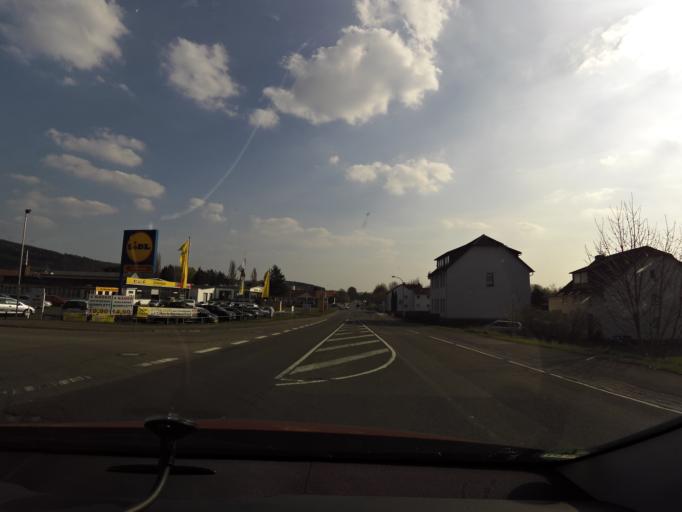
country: DE
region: Lower Saxony
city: Norten-Hardenberg
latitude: 51.6251
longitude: 9.9335
